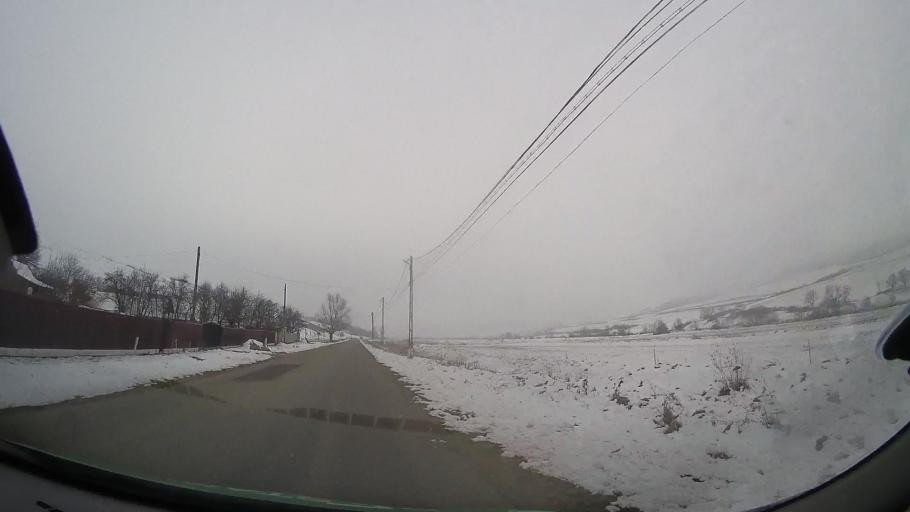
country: RO
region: Bacau
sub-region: Comuna Vultureni
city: Vultureni
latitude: 46.3185
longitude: 27.2929
